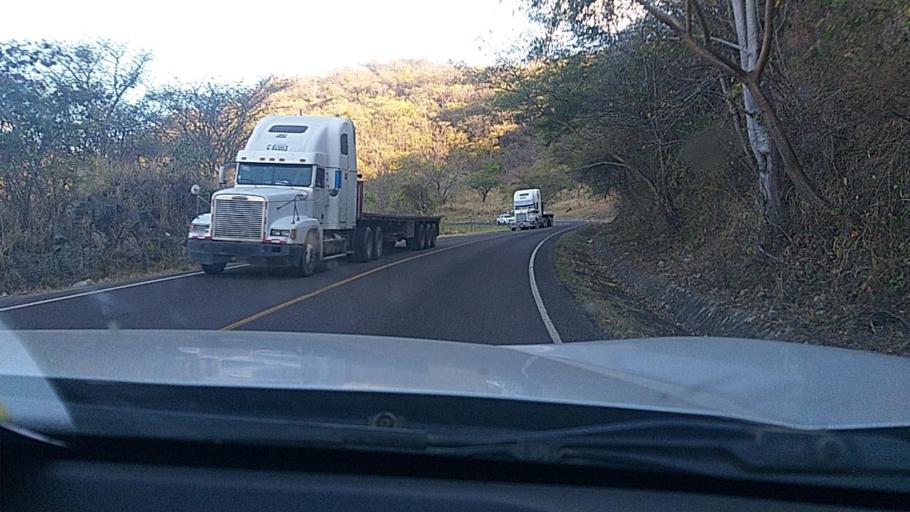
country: NI
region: Esteli
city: Condega
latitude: 13.2584
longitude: -86.3546
